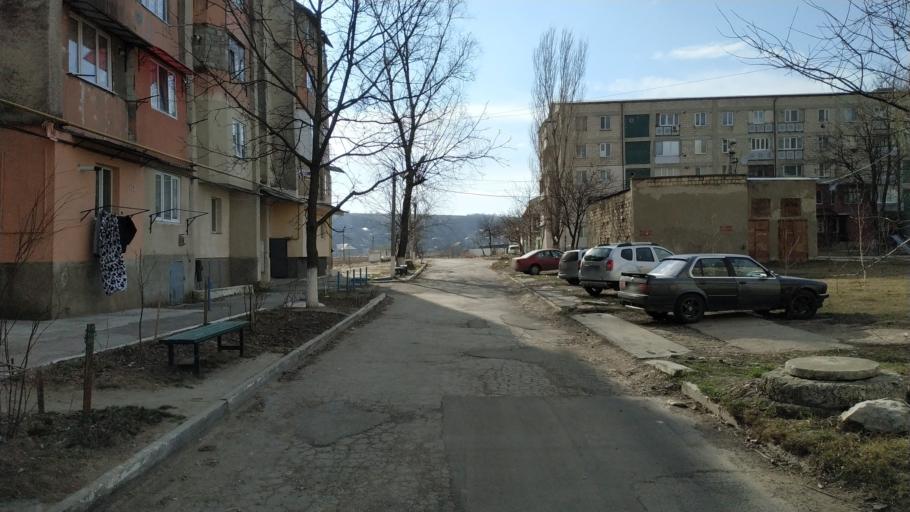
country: MD
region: Laloveni
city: Ialoveni
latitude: 46.9396
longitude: 28.7812
